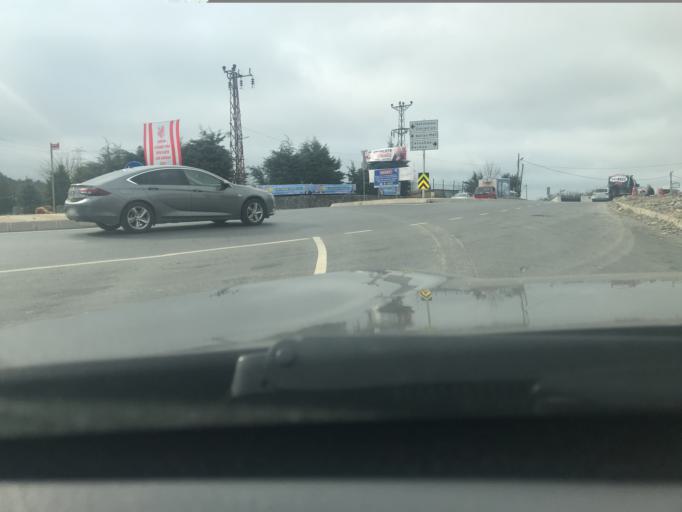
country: TR
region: Istanbul
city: Umraniye
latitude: 41.0562
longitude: 29.1687
